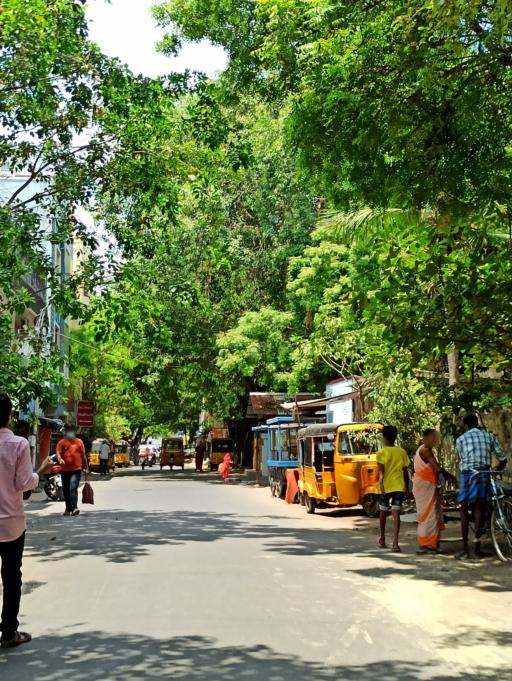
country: IN
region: Tamil Nadu
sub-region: Chennai
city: Chetput
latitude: 13.0564
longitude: 80.2293
